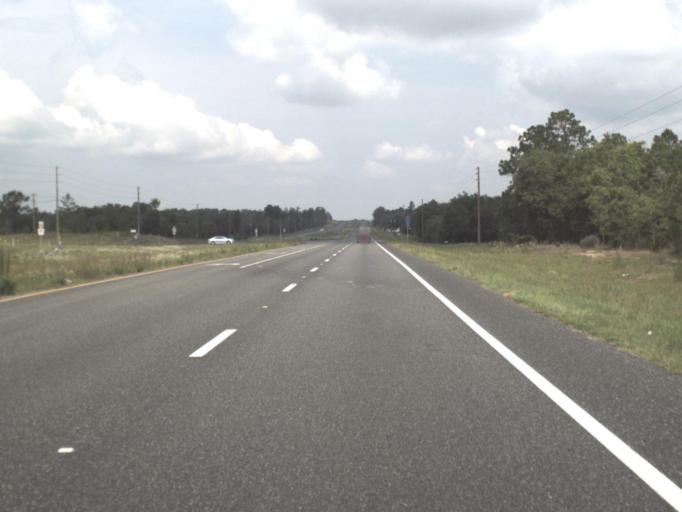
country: US
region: Florida
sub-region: Levy County
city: East Bronson
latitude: 29.4217
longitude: -82.5760
